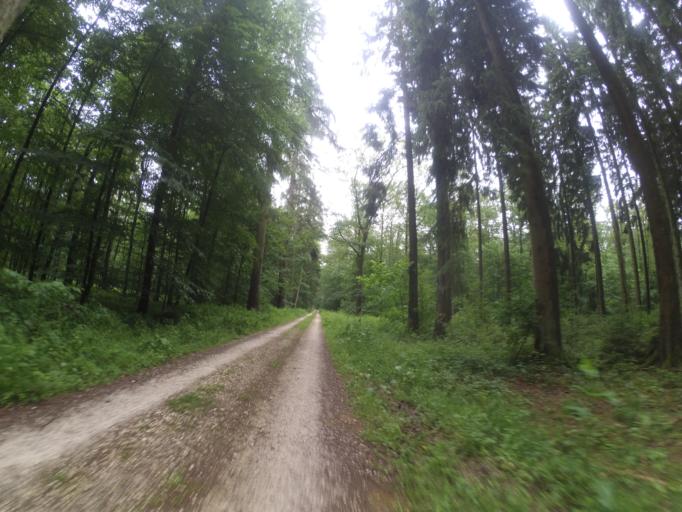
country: DE
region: Baden-Wuerttemberg
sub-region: Tuebingen Region
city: Borslingen
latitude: 48.5128
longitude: 10.0645
